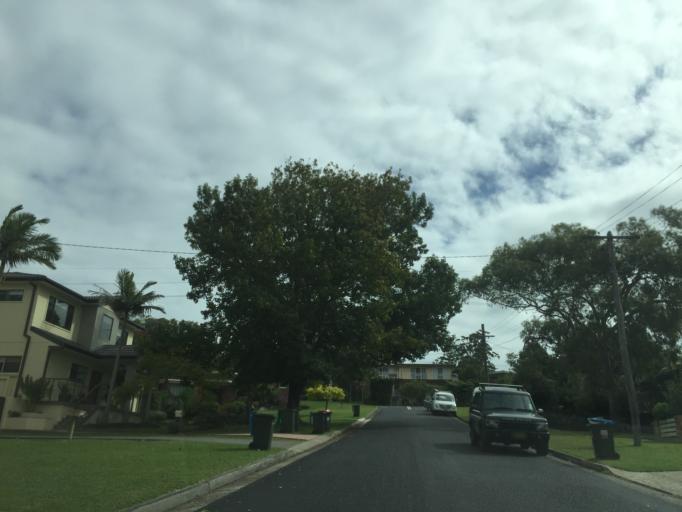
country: AU
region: New South Wales
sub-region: Pittwater
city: Warriewood
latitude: -33.6981
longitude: 151.2838
